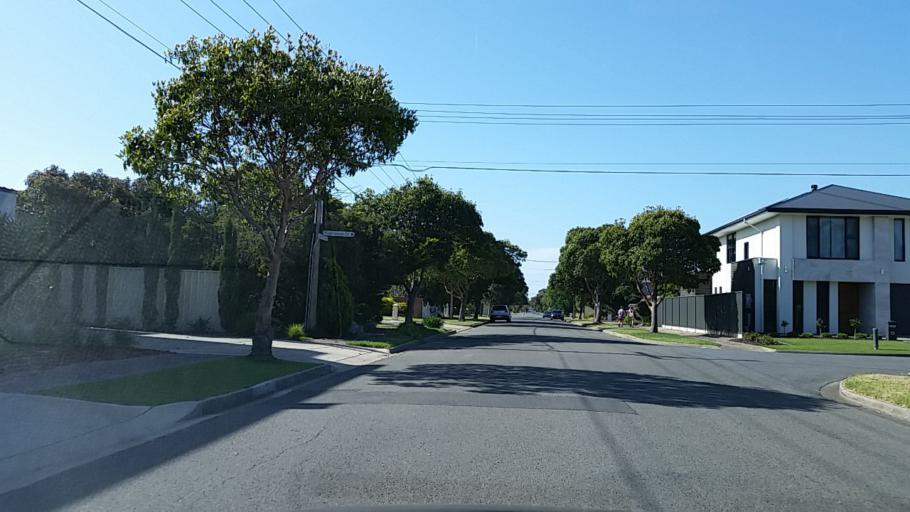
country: AU
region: South Australia
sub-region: Charles Sturt
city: Grange
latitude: -34.9114
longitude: 138.5020
